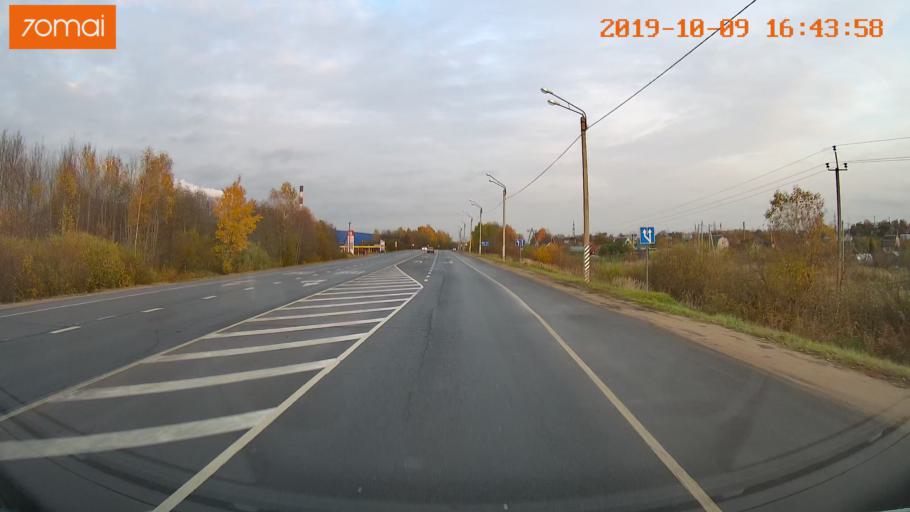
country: RU
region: Kostroma
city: Volgorechensk
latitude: 57.4524
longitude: 41.1335
